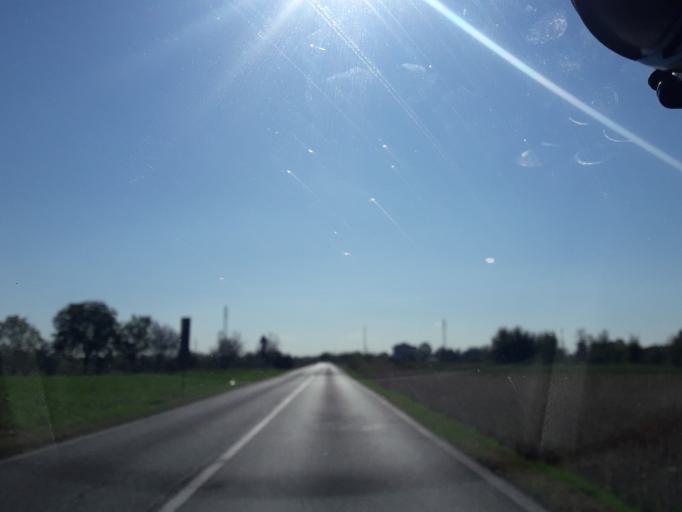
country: IT
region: Friuli Venezia Giulia
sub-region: Provincia di Udine
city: Udine
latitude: 46.0731
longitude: 13.2805
